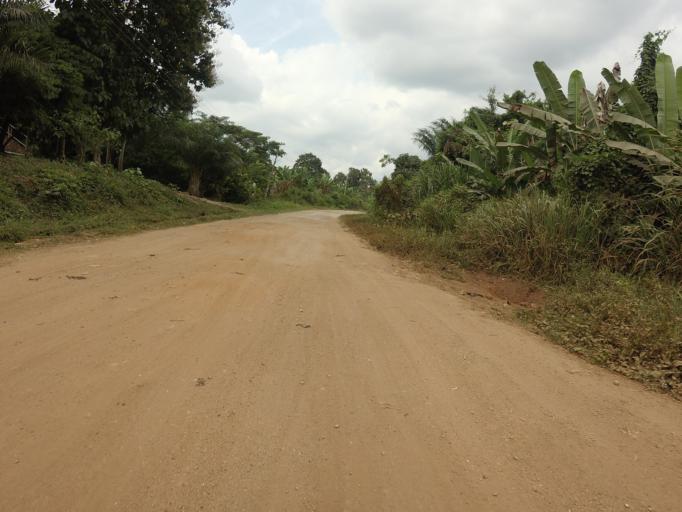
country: GH
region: Volta
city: Ho
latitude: 6.6470
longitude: 0.3381
